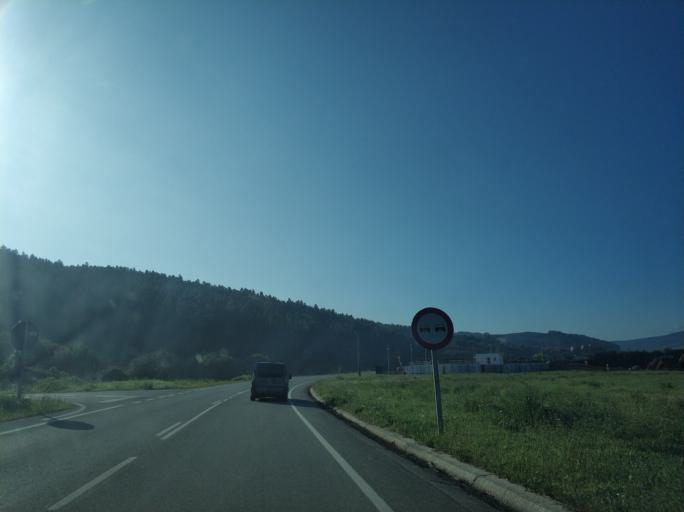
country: ES
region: Cantabria
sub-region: Provincia de Cantabria
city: Polanco
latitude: 43.3810
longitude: -3.9668
